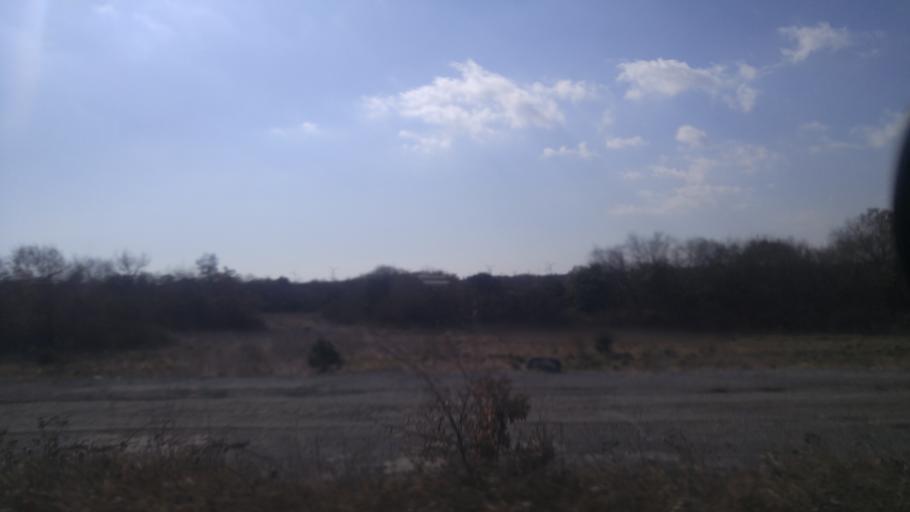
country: TR
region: Istanbul
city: Canta
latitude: 41.1675
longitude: 28.0985
